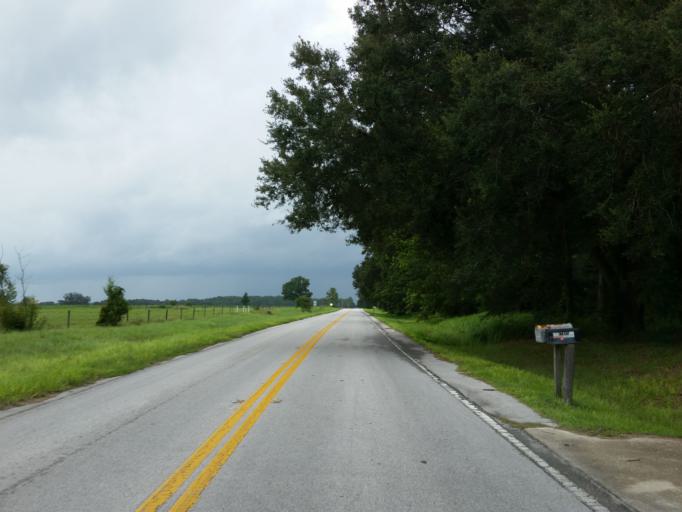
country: US
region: Florida
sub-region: Levy County
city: Williston
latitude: 29.3890
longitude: -82.4056
